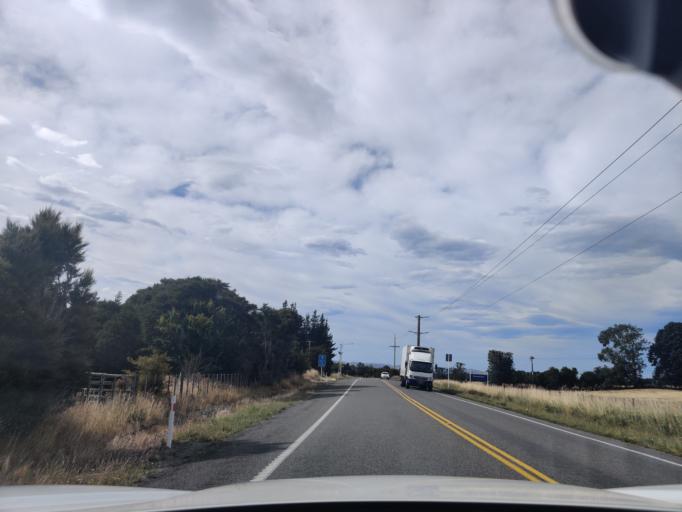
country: NZ
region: Wellington
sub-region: Masterton District
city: Masterton
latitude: -40.8415
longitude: 175.6312
